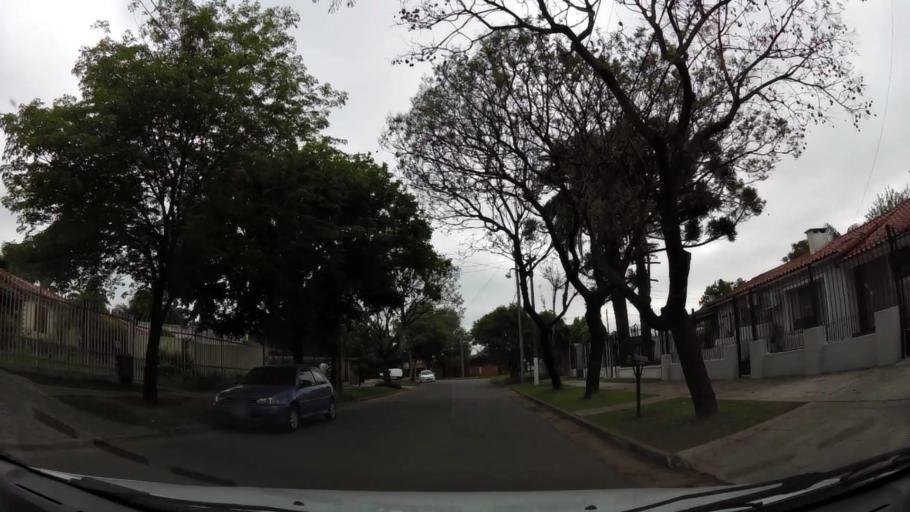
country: AR
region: Buenos Aires
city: San Justo
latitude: -34.7124
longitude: -58.5387
